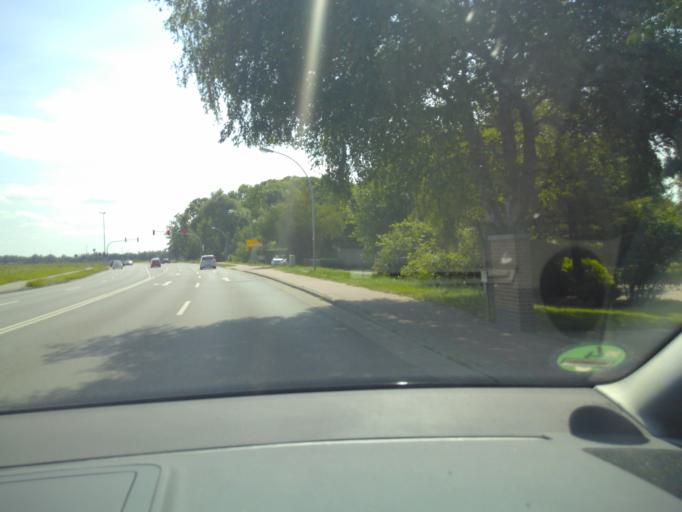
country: DE
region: Lower Saxony
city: Cuxhaven
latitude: 53.8364
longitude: 8.6817
